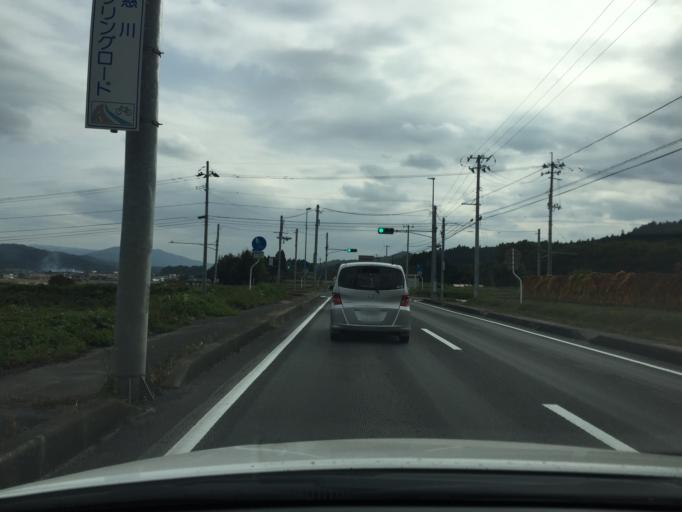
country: JP
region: Fukushima
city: Ishikawa
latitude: 37.0092
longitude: 140.3849
